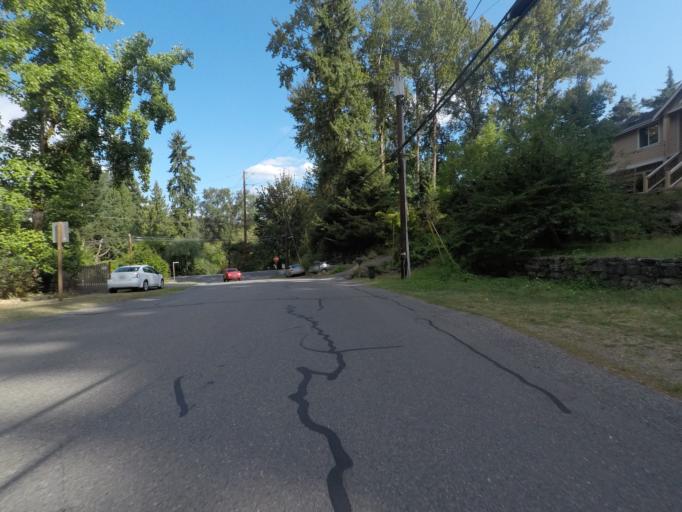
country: US
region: Washington
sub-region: King County
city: Kenmore
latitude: 47.7700
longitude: -122.2492
